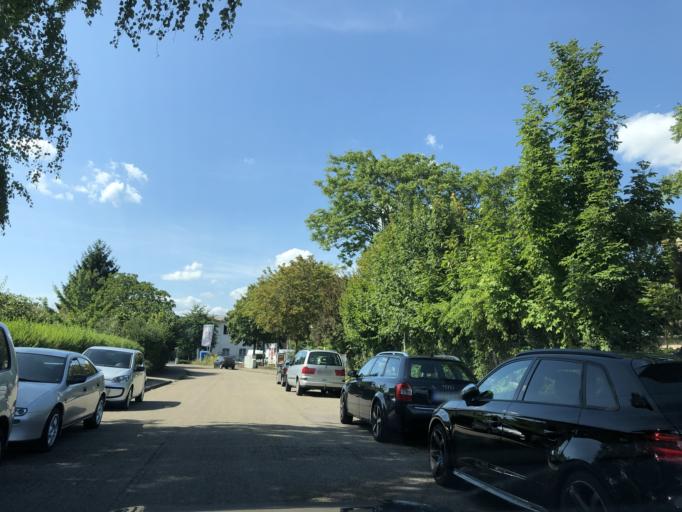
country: DE
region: Baden-Wuerttemberg
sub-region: Karlsruhe Region
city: Rastatt
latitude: 48.8587
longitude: 8.2191
